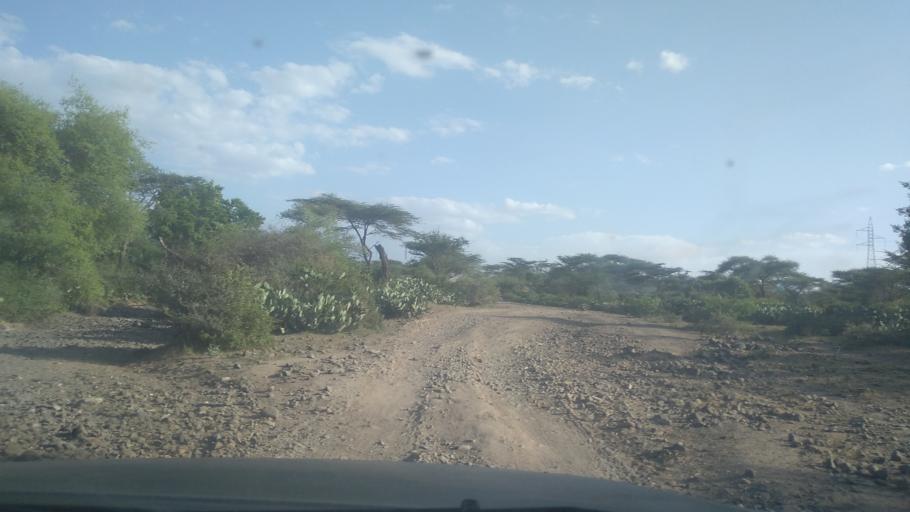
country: ET
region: Oromiya
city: Hirna
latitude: 9.4221
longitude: 40.9623
